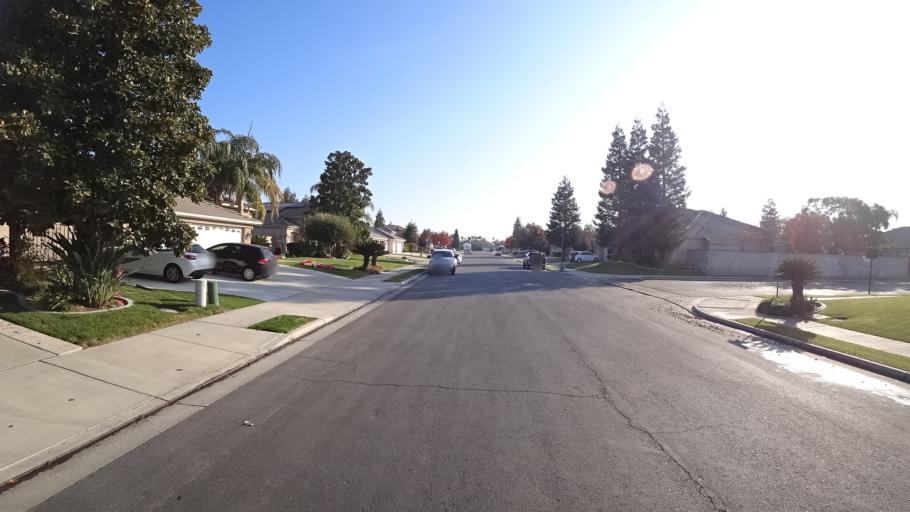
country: US
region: California
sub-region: Kern County
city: Greenacres
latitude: 35.3641
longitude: -119.1220
